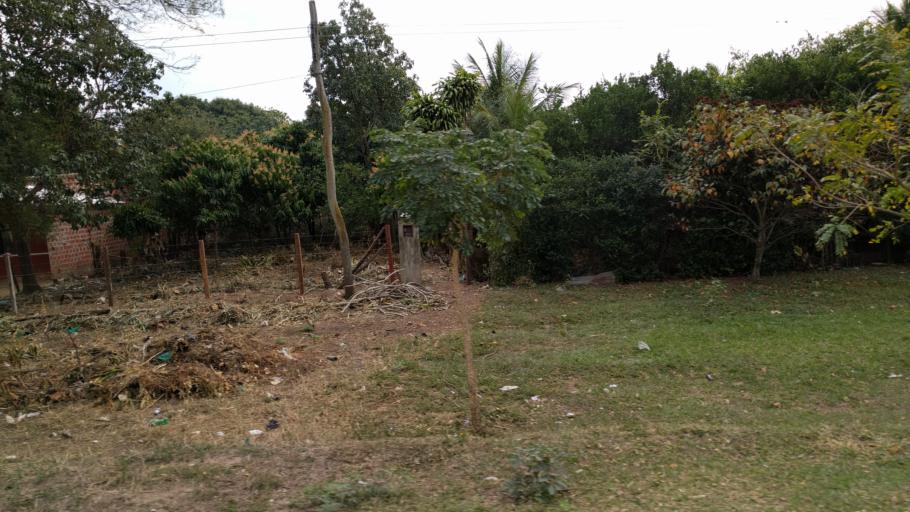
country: BO
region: Santa Cruz
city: Jorochito
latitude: -18.0455
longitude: -63.4179
